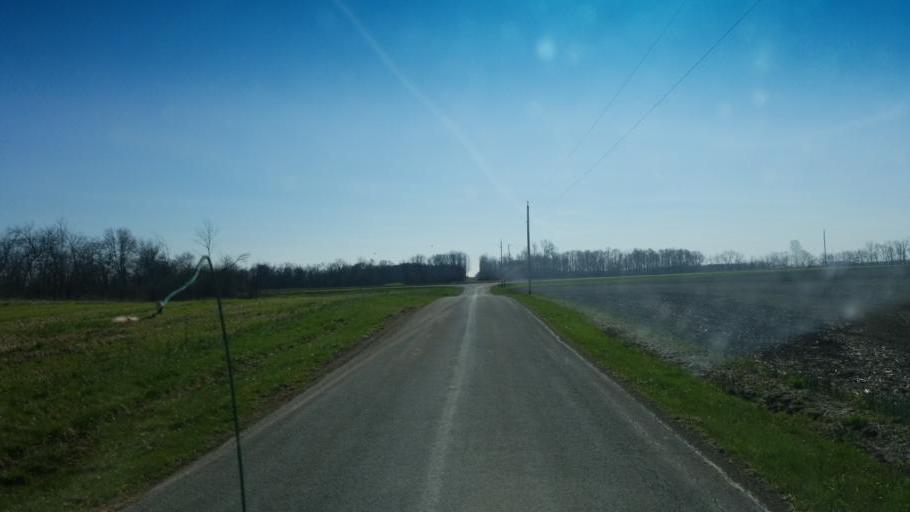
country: US
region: Ohio
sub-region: Hardin County
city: Forest
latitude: 40.7015
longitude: -83.4978
